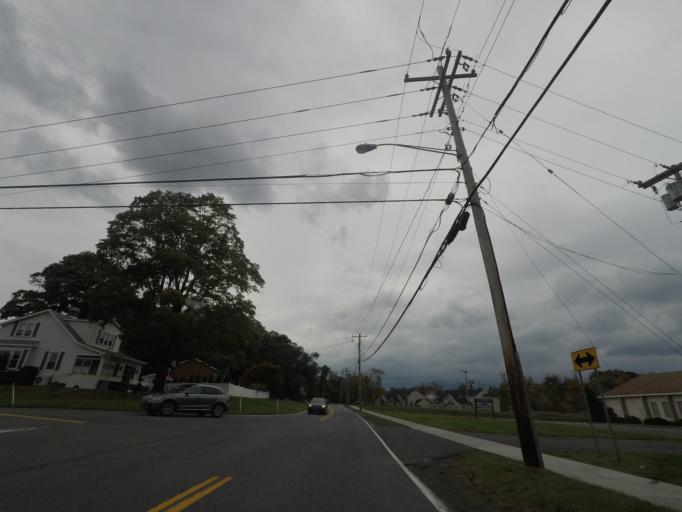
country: US
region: New York
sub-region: Albany County
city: McKownville
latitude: 42.6629
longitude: -73.8428
